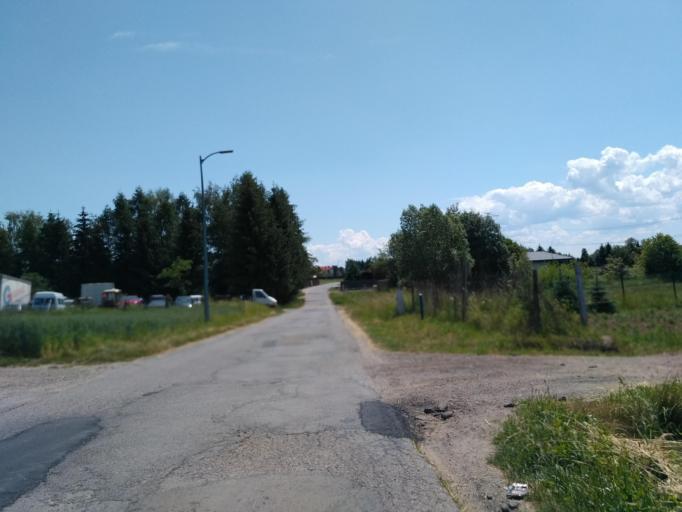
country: PL
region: Subcarpathian Voivodeship
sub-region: Powiat krosnienski
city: Korczyna
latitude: 49.7083
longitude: 21.7927
